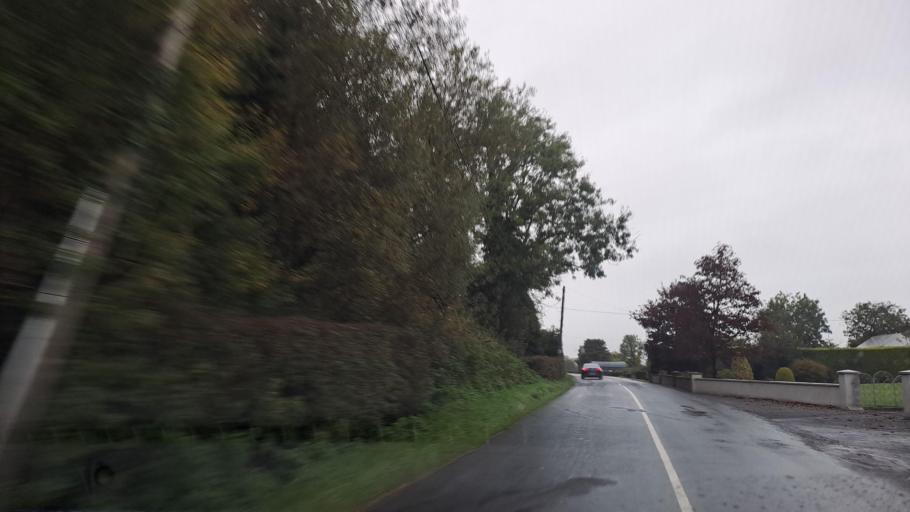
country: IE
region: Ulster
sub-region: County Monaghan
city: Monaghan
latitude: 54.2155
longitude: -6.9094
